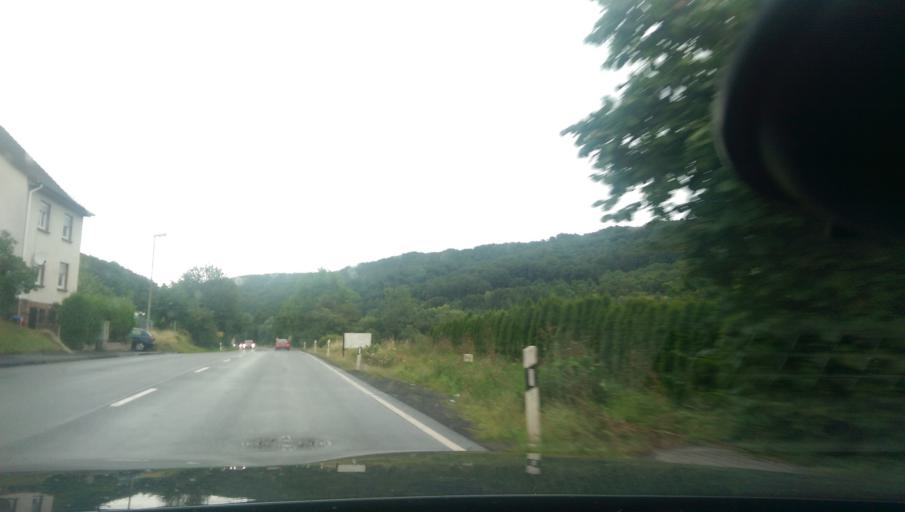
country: DE
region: Hesse
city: Witzenhausen
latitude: 51.2959
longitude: 9.8487
